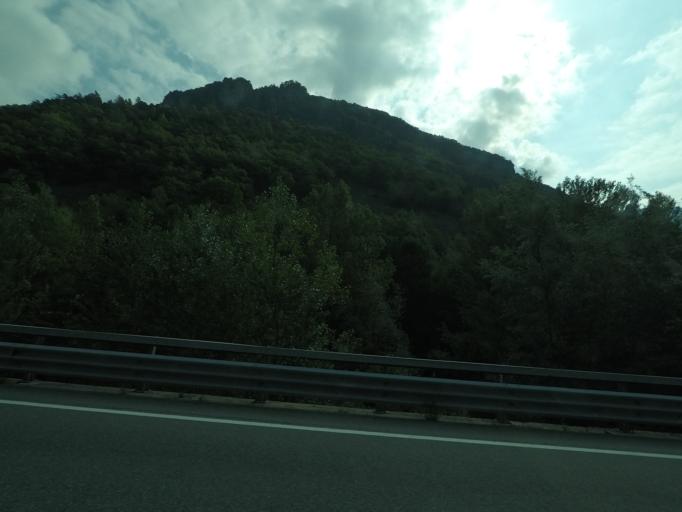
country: IT
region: Aosta Valley
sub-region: Valle d'Aosta
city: Antey-Saint-Andre
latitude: 45.7815
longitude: 7.5905
